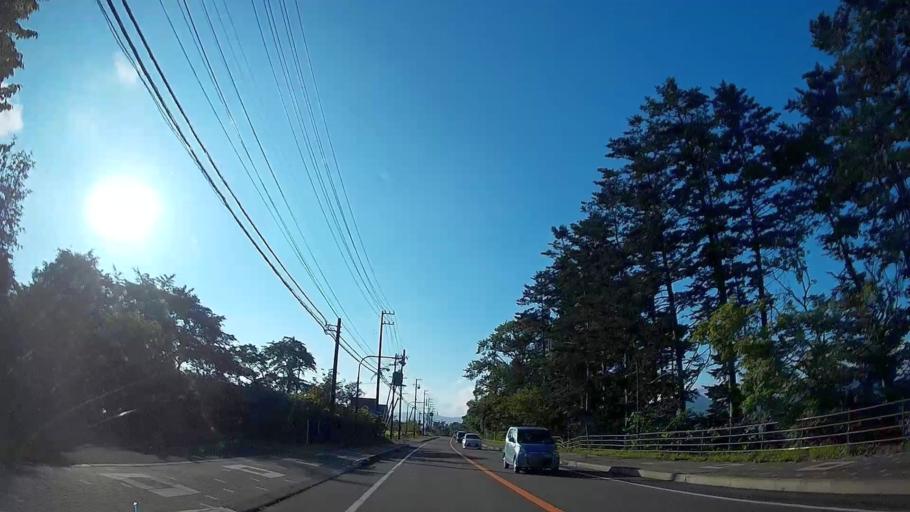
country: JP
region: Hokkaido
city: Date
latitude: 42.5574
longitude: 140.8555
